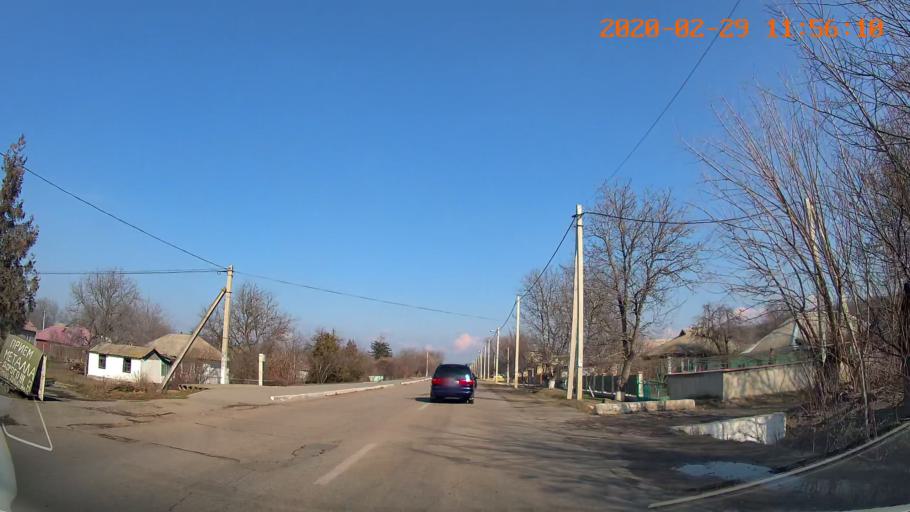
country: MD
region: Telenesti
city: Ribnita
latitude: 47.7945
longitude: 29.0007
